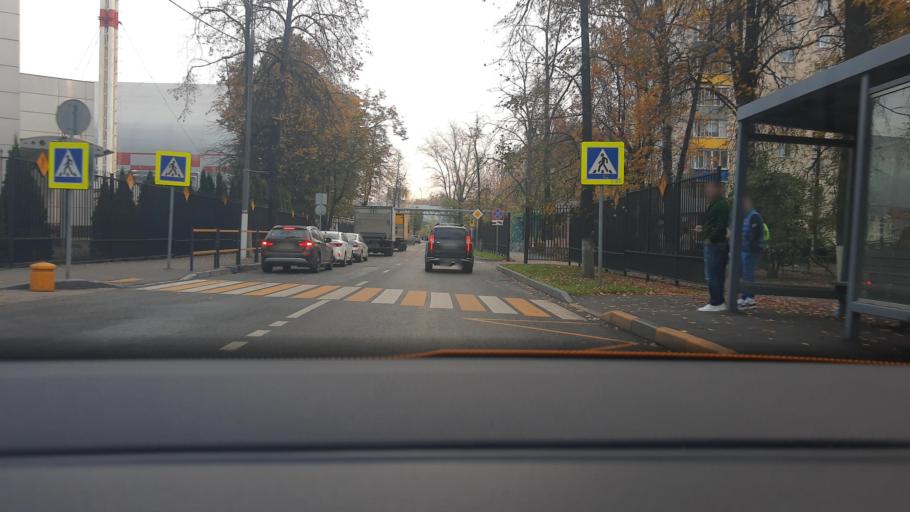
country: RU
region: Moscow
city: Khimki
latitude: 55.8850
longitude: 37.4527
